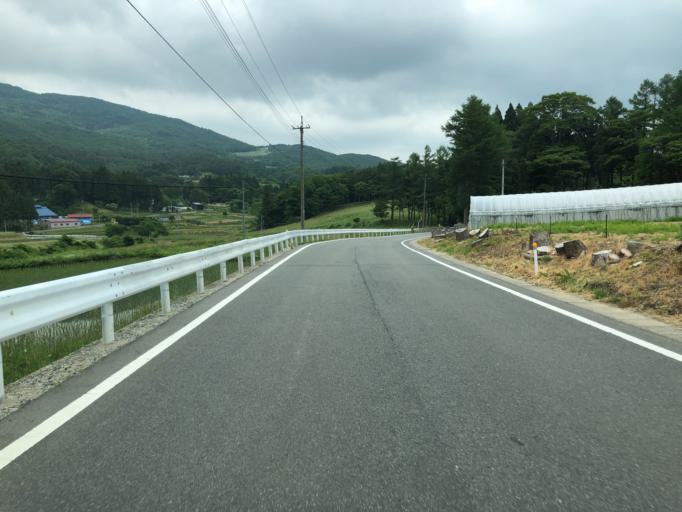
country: JP
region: Fukushima
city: Funehikimachi-funehiki
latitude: 37.3859
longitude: 140.7291
